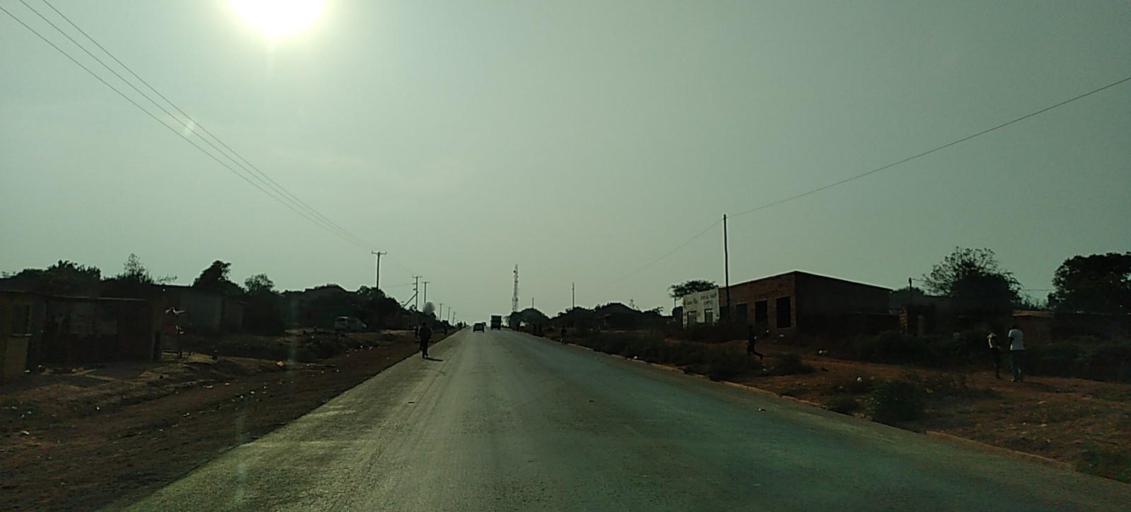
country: ZM
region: North-Western
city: Solwezi
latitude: -12.1907
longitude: 26.4386
